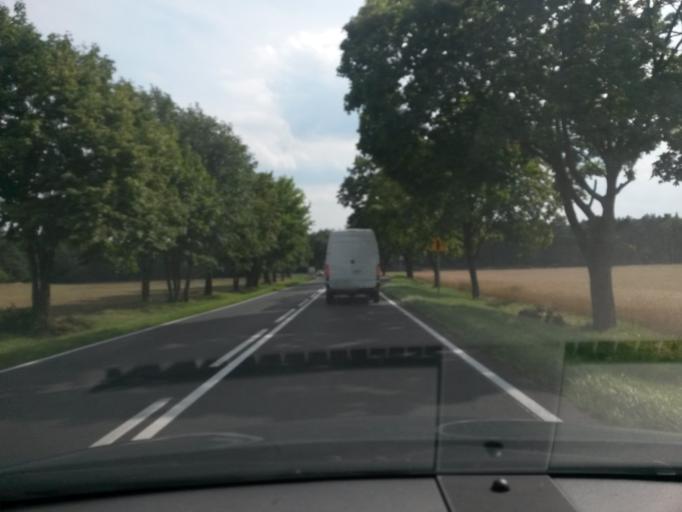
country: PL
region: Greater Poland Voivodeship
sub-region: Powiat sremski
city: Srem
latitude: 52.1553
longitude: 17.0352
